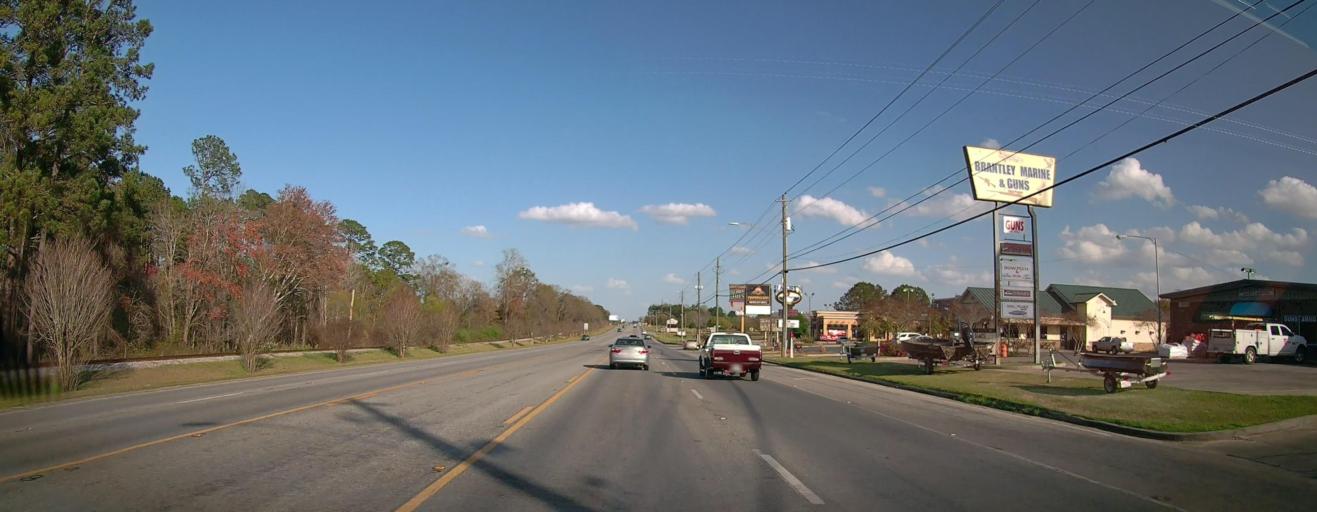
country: US
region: Georgia
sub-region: Toombs County
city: Vidalia
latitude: 32.2064
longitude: -82.3727
